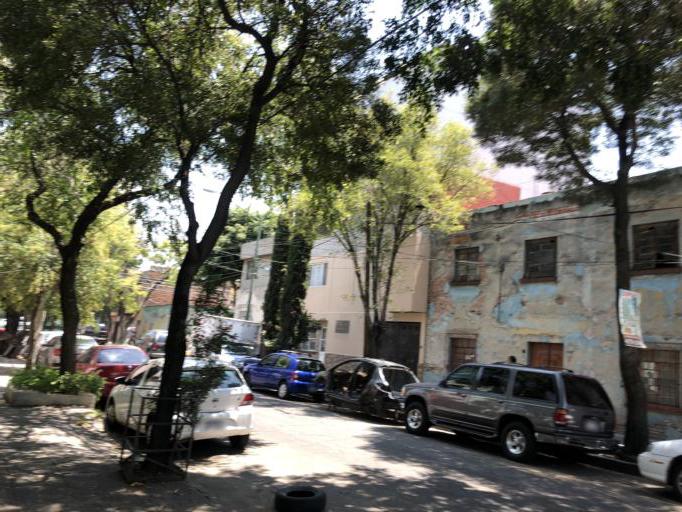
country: MX
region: Mexico City
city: Cuauhtemoc
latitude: 19.4570
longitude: -99.1364
